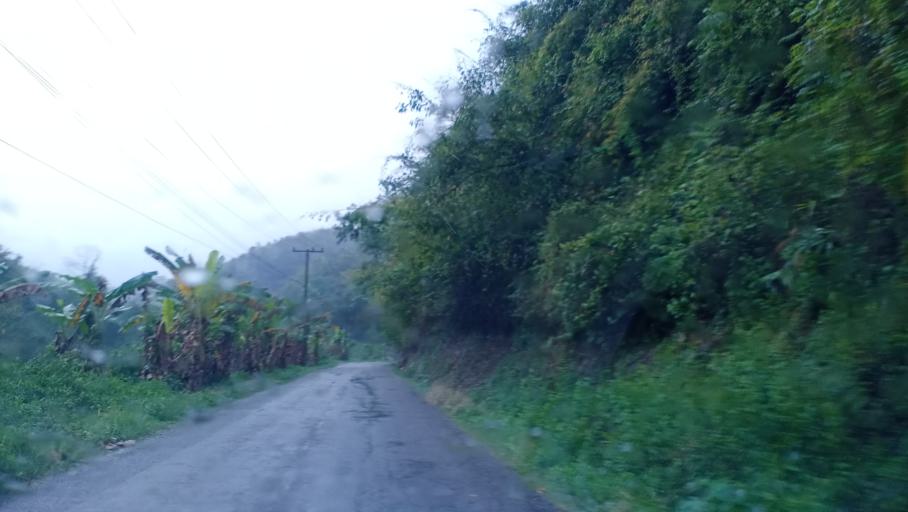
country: LA
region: Phongsali
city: Khoa
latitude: 21.0618
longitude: 102.4712
